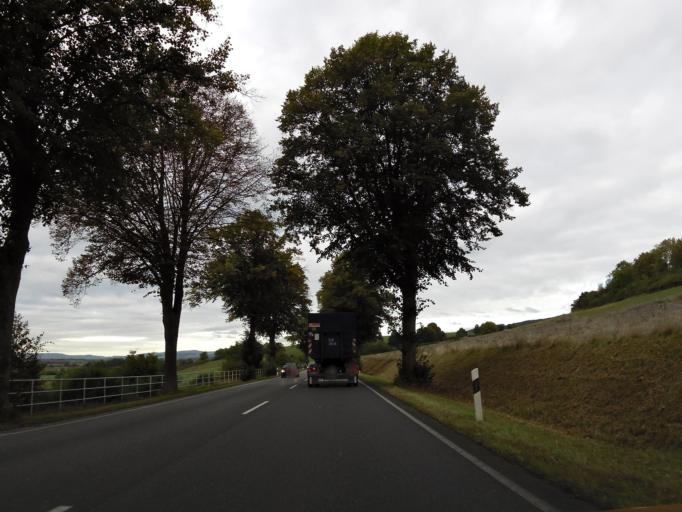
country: DE
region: Lower Saxony
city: Kreiensen
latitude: 51.7737
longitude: 9.9443
